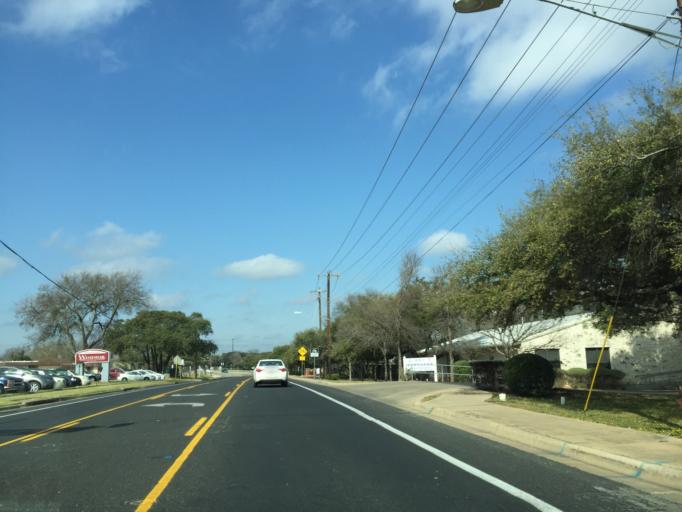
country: US
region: Texas
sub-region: Williamson County
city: Jollyville
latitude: 30.4180
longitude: -97.7430
